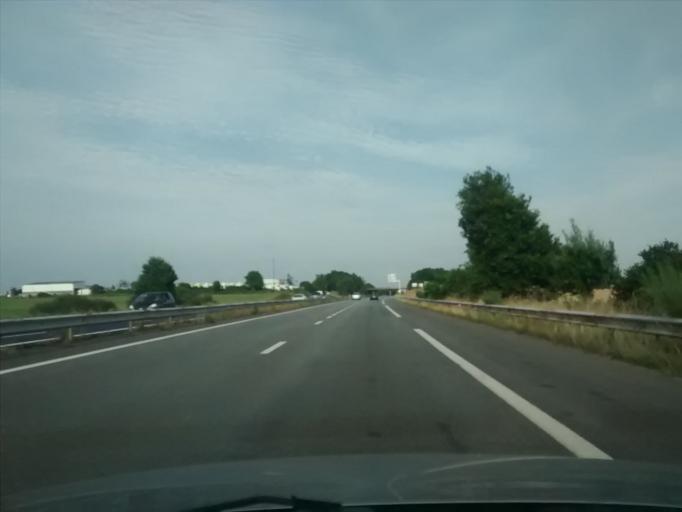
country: FR
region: Brittany
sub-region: Departement d'Ille-et-Vilaine
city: Etrelles
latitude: 48.0722
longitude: -1.2061
